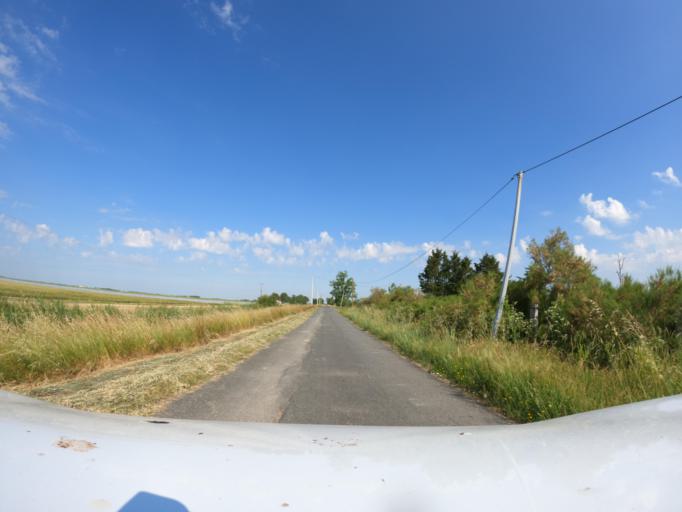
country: FR
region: Pays de la Loire
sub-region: Departement de la Vendee
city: Champagne-les-Marais
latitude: 46.3542
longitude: -1.1210
